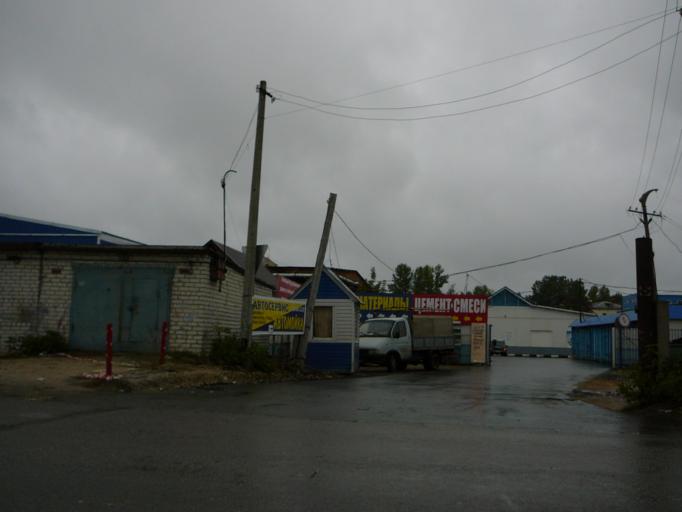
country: RU
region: Moskovskaya
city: Shatura
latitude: 55.5738
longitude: 39.5278
